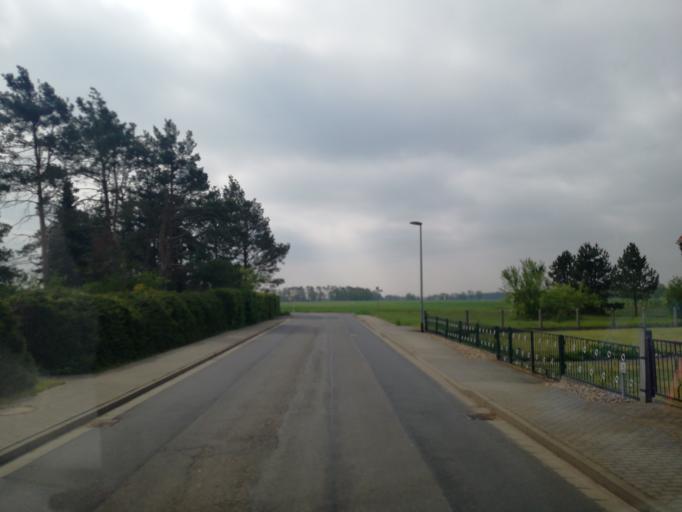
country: DE
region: Saxony
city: Beilrode
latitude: 51.6340
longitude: 13.1204
